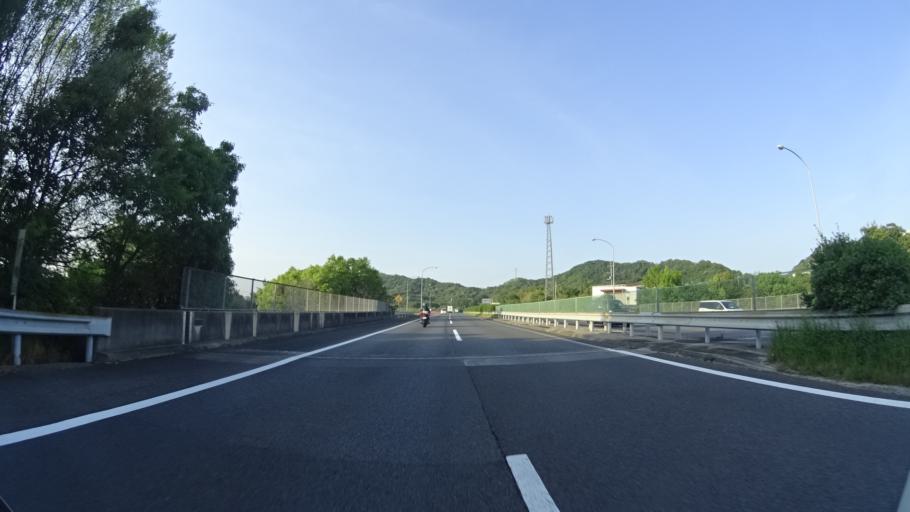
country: JP
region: Kagawa
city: Kan'onjicho
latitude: 34.1483
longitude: 133.7152
